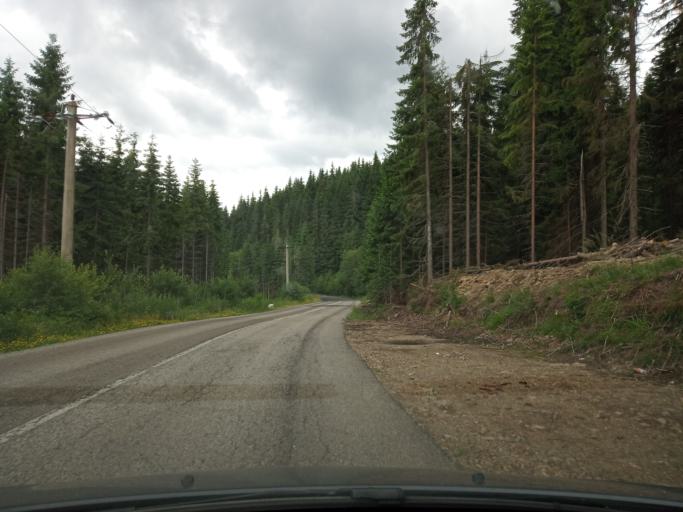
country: RO
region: Gorj
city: Novaci-Straini
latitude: 45.4266
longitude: 23.6868
